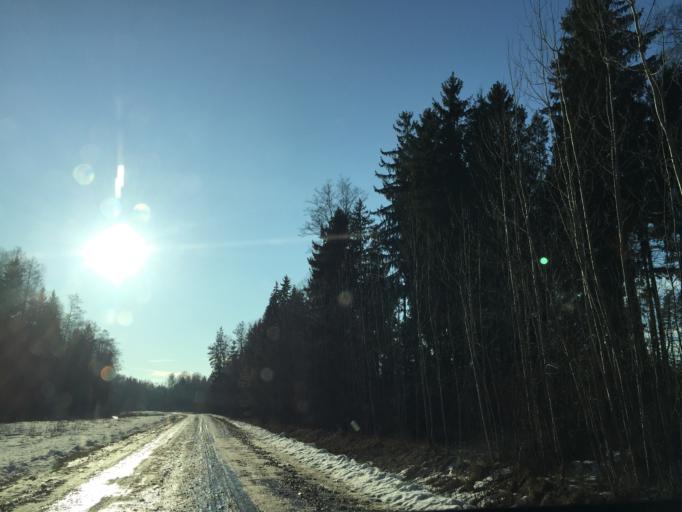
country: LV
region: Lecava
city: Iecava
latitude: 56.6892
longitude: 24.0766
